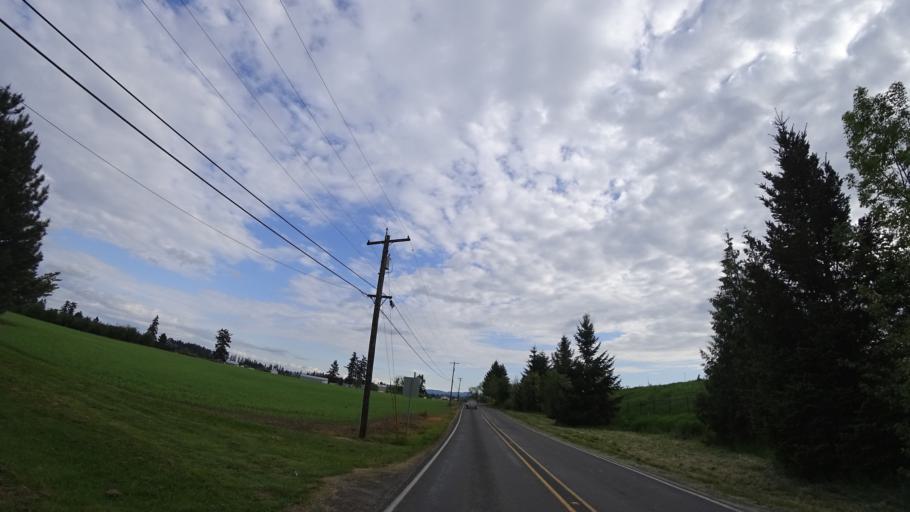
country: US
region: Oregon
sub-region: Washington County
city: Hillsboro
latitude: 45.4907
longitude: -122.9701
